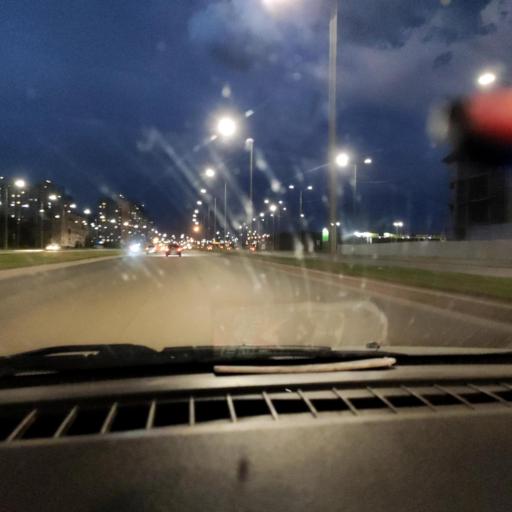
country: RU
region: Orenburg
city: Orenburg
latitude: 51.8050
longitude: 55.1666
